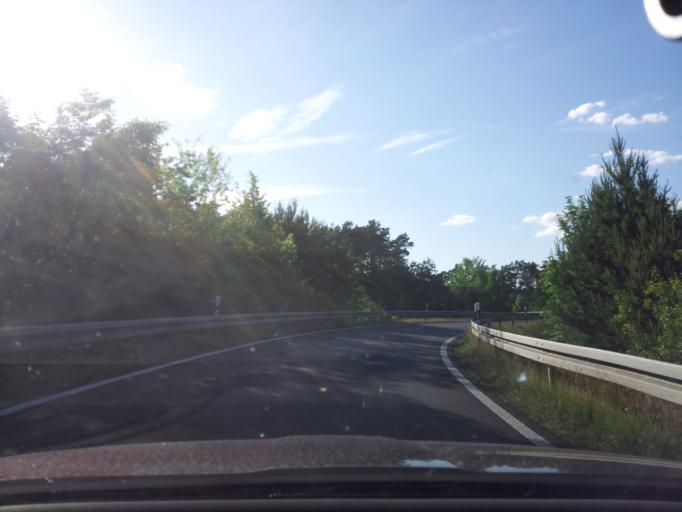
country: DE
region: Berlin
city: Wannsee
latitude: 52.3732
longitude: 13.1532
